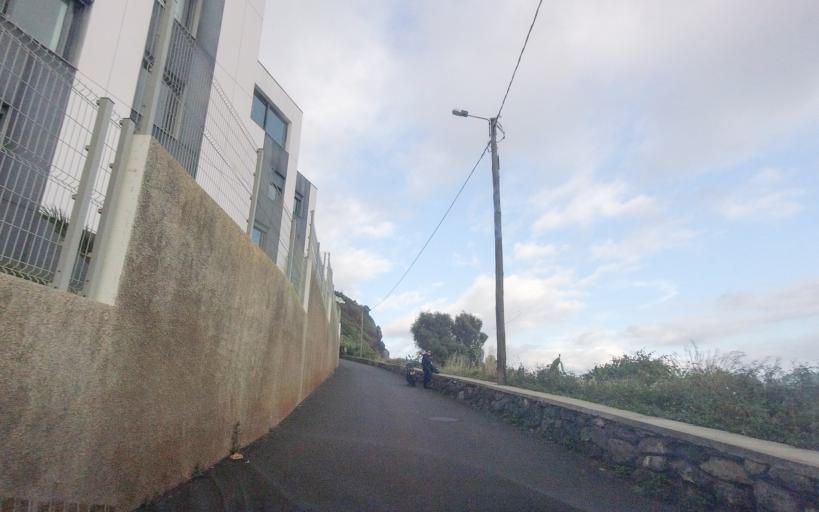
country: PT
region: Madeira
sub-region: Funchal
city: Funchal
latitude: 32.6464
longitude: -16.8840
